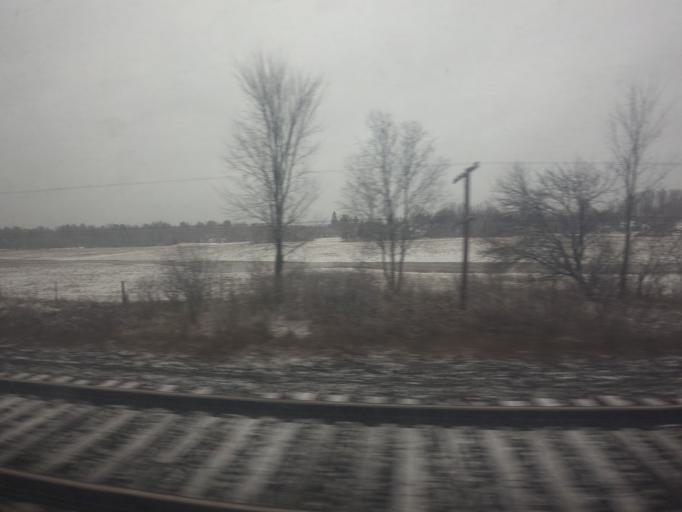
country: US
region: New York
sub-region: Jefferson County
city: Alexandria Bay
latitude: 44.5006
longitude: -75.8610
